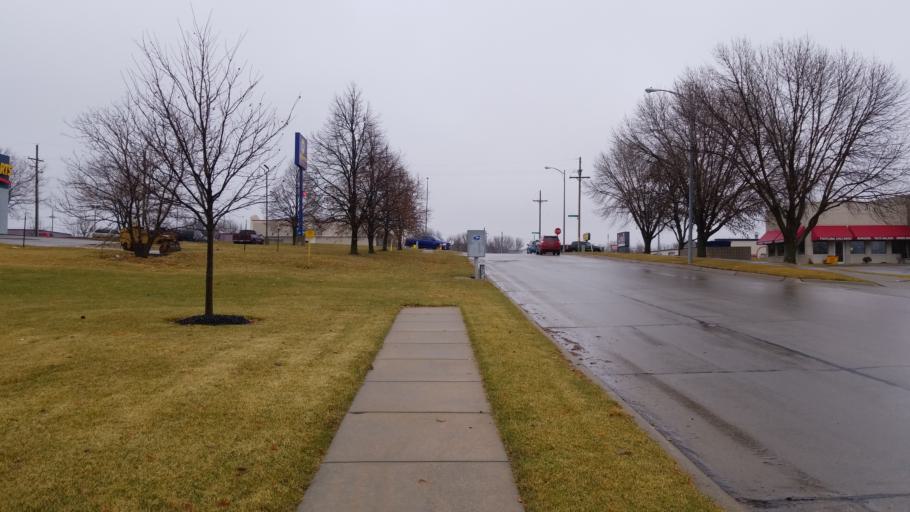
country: US
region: Nebraska
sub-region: Sarpy County
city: Offutt Air Force Base
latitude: 41.1584
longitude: -95.9455
